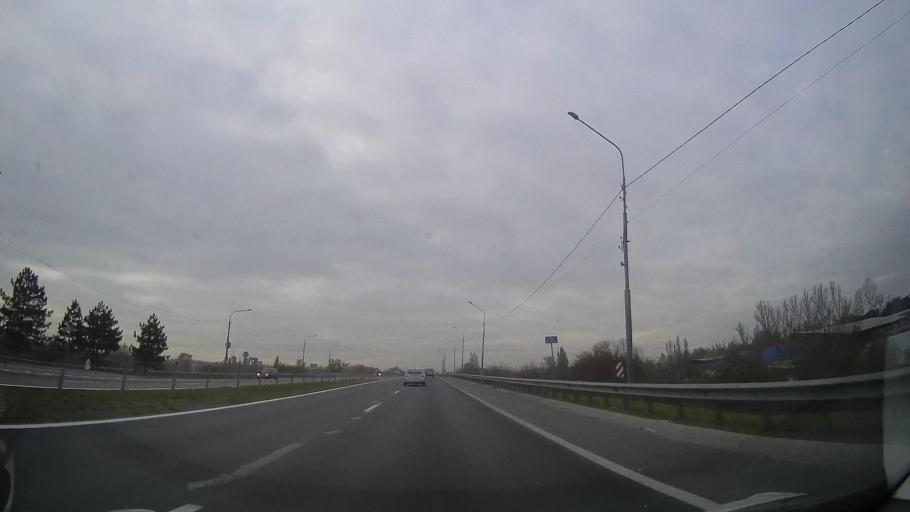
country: RU
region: Rostov
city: Bataysk
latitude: 47.1034
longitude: 39.7639
